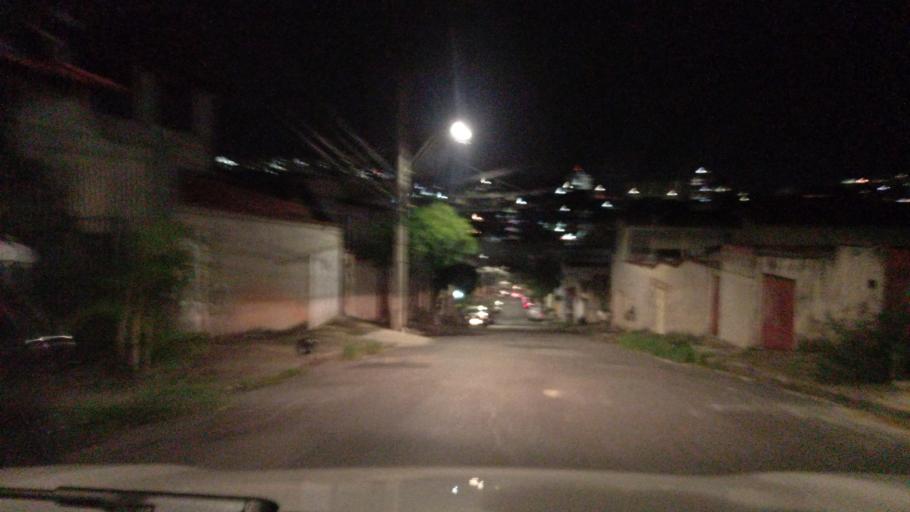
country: BR
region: Minas Gerais
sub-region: Belo Horizonte
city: Belo Horizonte
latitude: -19.8774
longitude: -43.9428
